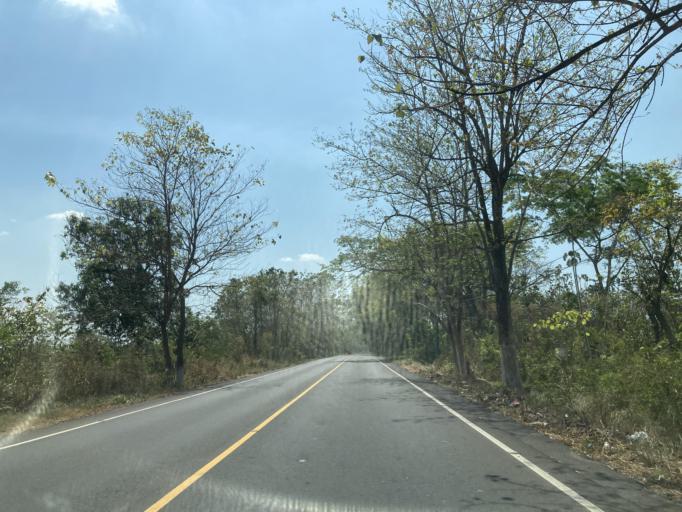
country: GT
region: Escuintla
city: Guanagazapa
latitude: 14.1887
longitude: -90.6936
